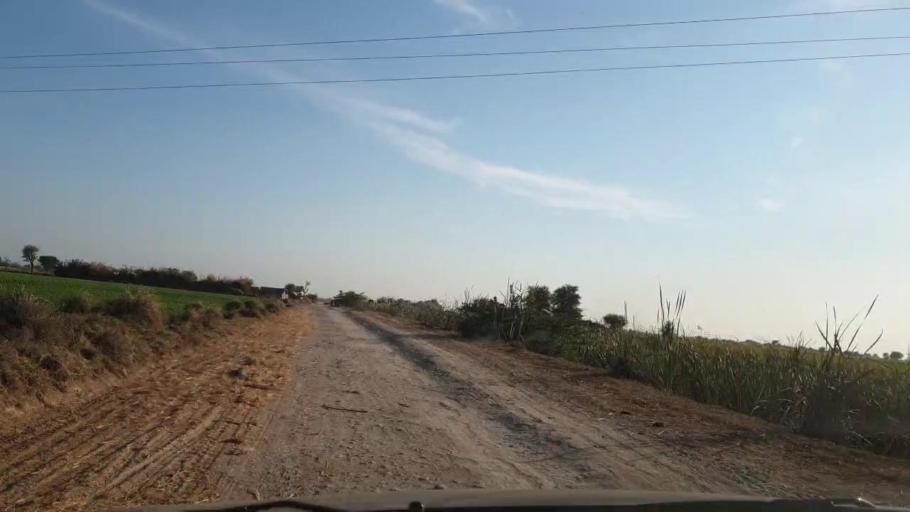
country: PK
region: Sindh
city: Khadro
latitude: 26.2184
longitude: 68.7407
